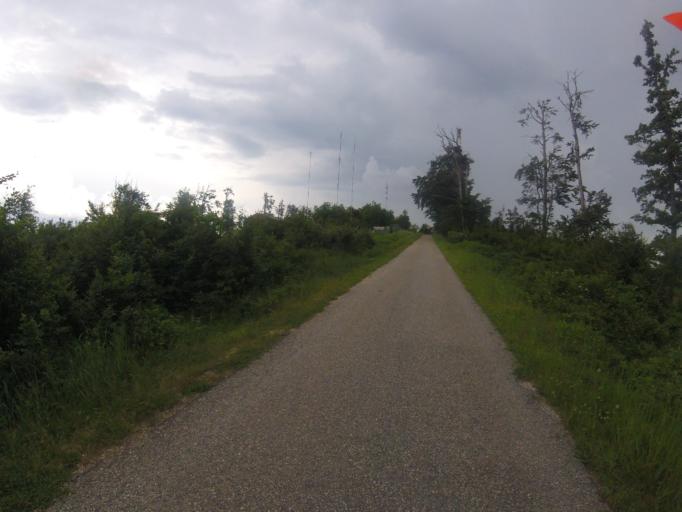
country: HU
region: Veszprem
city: Urkut
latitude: 47.0479
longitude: 17.6558
